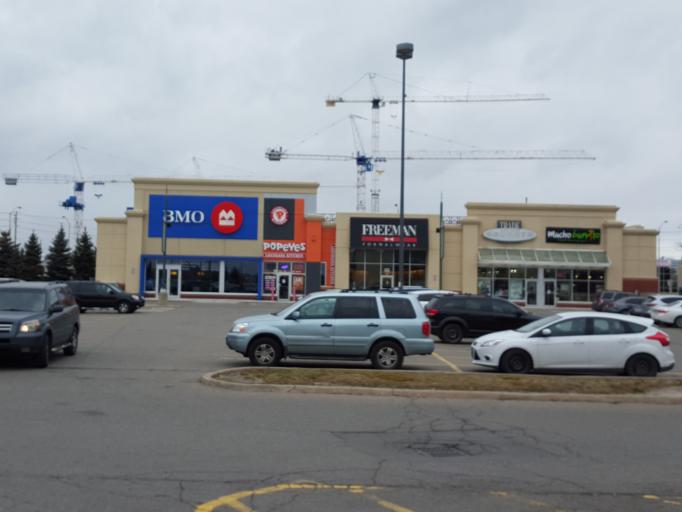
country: CA
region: Ontario
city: Concord
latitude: 43.7884
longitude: -79.5456
